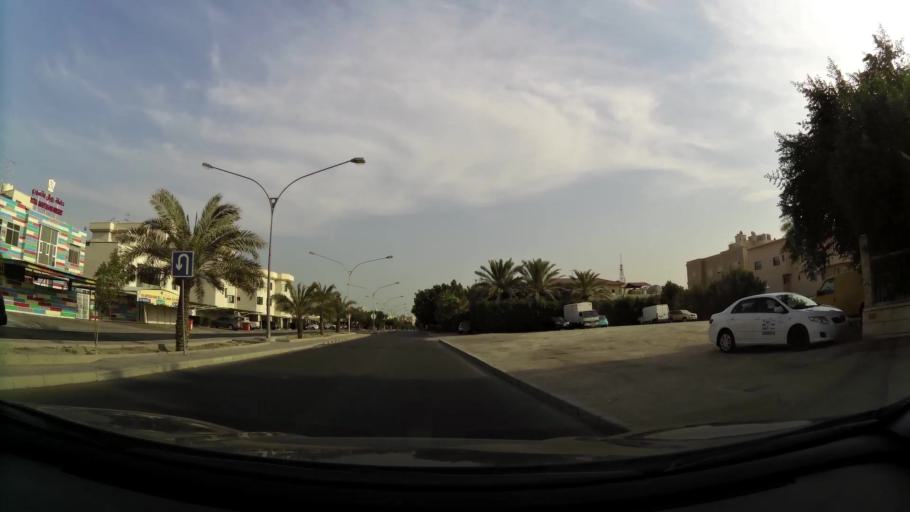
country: KW
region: Muhafazat Hawalli
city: Hawalli
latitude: 29.3134
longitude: 48.0116
